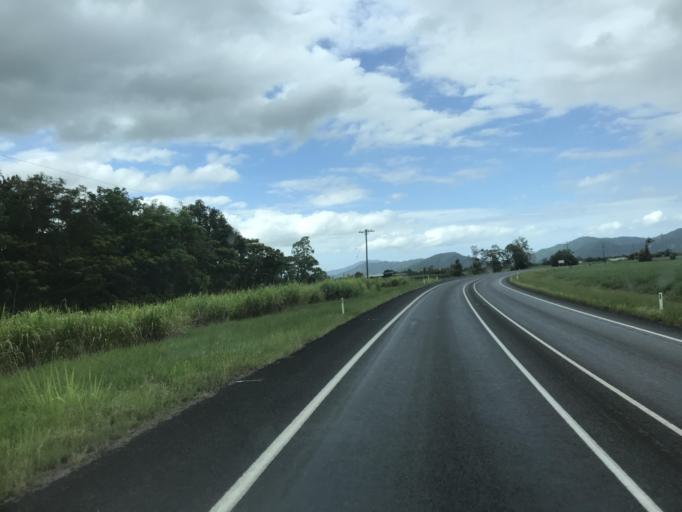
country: AU
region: Queensland
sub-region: Cassowary Coast
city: Innisfail
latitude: -17.7807
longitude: 146.0279
